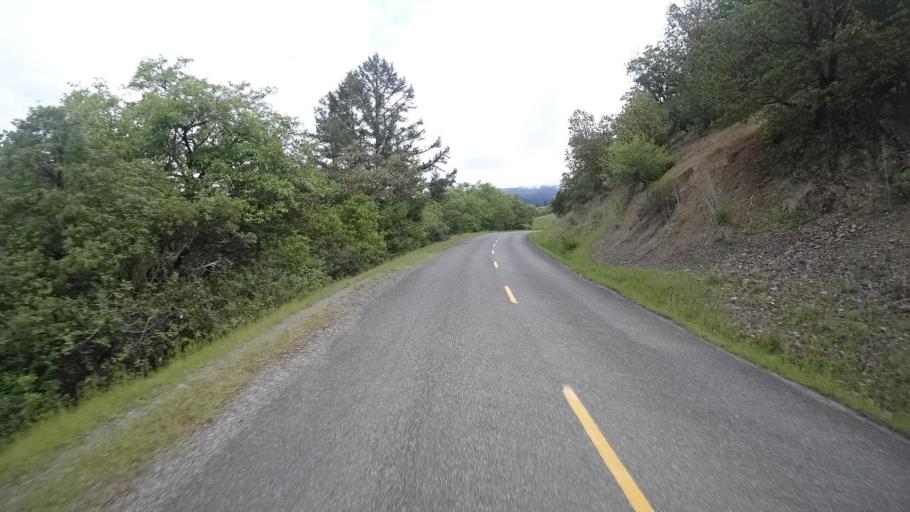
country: US
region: California
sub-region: Humboldt County
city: Redway
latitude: 40.2081
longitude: -123.5961
